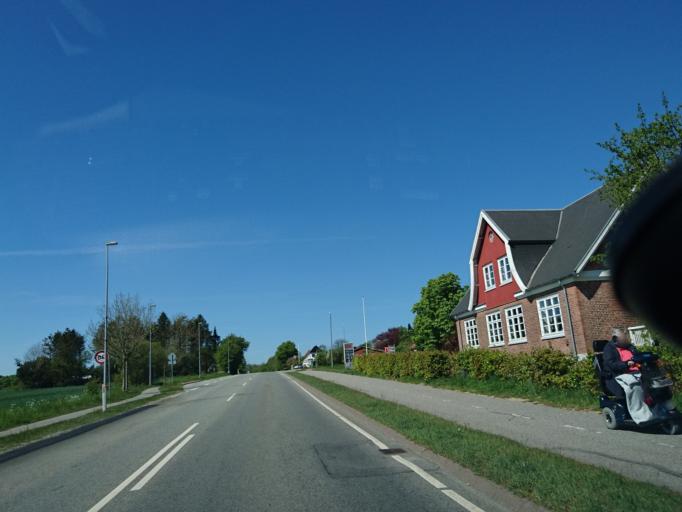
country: DK
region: North Denmark
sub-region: Hjorring Kommune
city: Sindal
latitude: 57.4703
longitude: 10.1927
